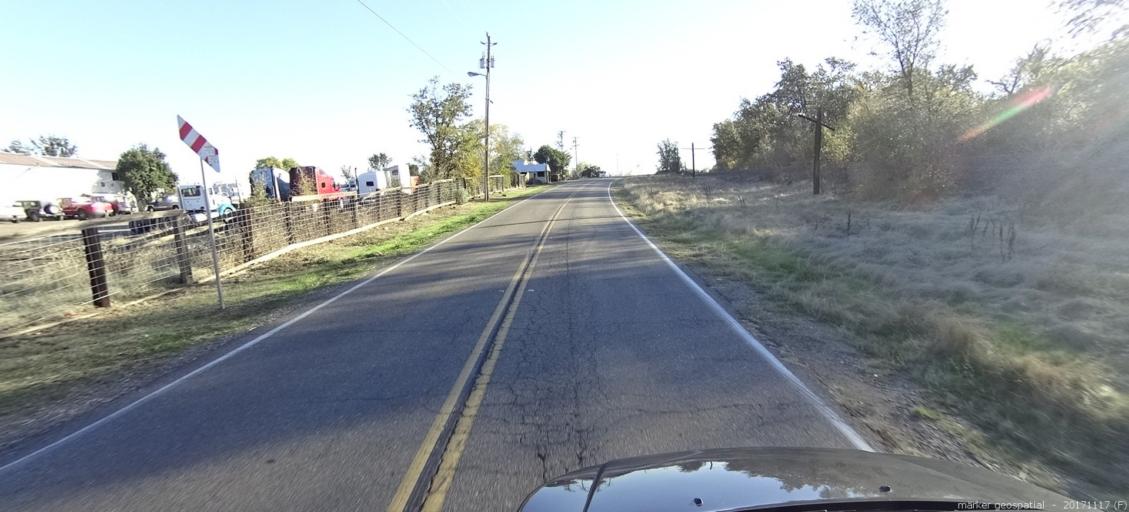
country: US
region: California
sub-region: Shasta County
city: Cottonwood
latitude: 40.4067
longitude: -122.2444
